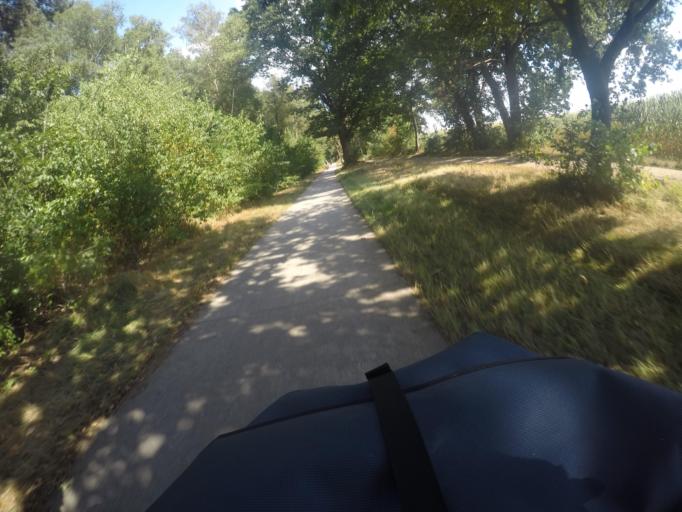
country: NL
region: Gelderland
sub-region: Gemeente Renkum
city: Renkum
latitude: 52.0164
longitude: 5.7327
